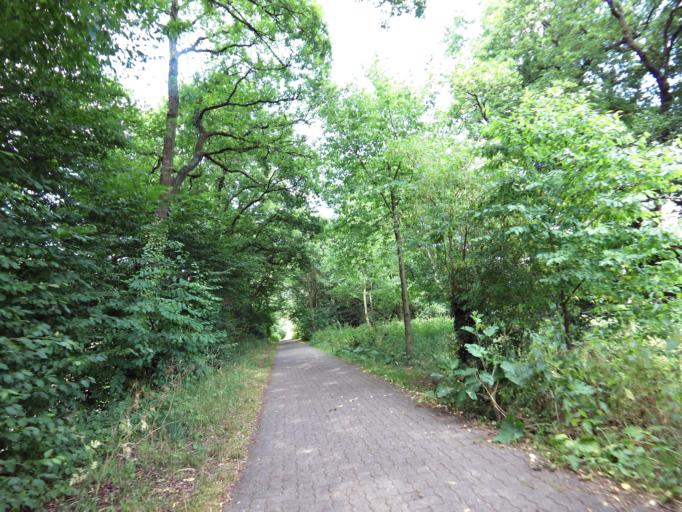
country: DE
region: North Rhine-Westphalia
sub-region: Regierungsbezirk Koln
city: Herzogenrath
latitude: 50.8574
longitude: 6.0881
